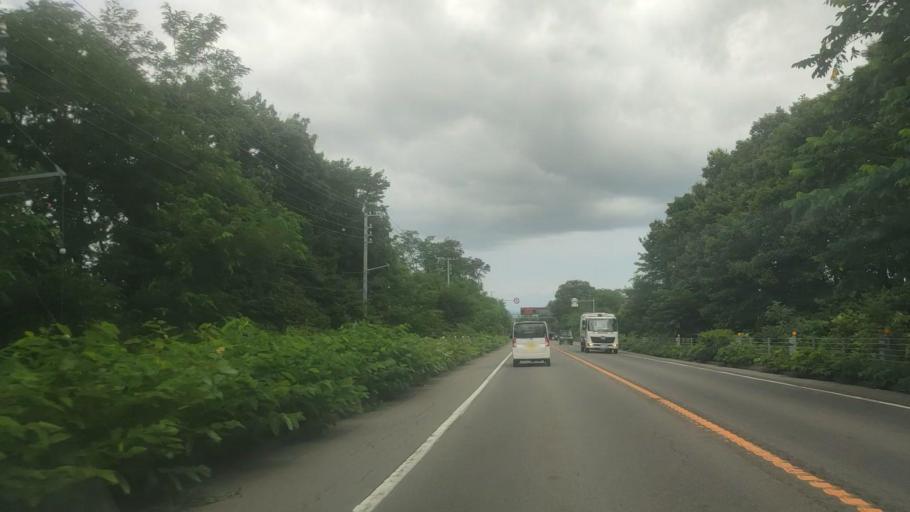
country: JP
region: Hokkaido
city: Nanae
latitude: 42.0725
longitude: 140.6023
